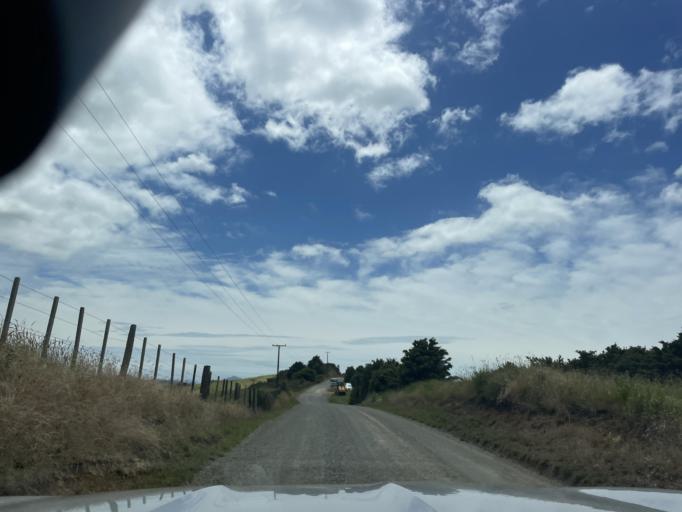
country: NZ
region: Auckland
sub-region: Auckland
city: Wellsford
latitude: -36.1589
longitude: 174.5376
